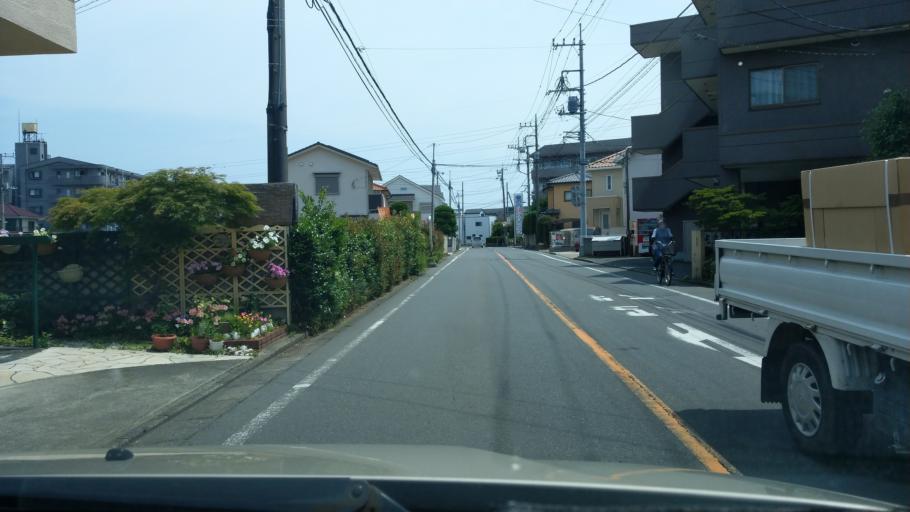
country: JP
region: Saitama
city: Saitama
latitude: 35.9087
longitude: 139.6390
